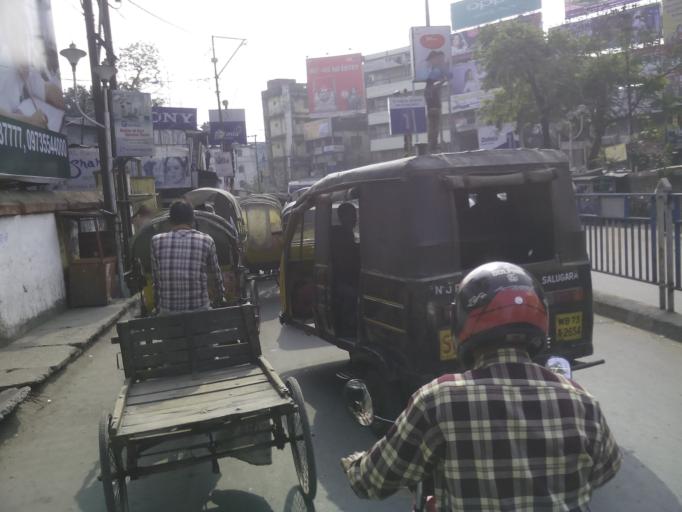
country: IN
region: West Bengal
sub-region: Darjiling
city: Shiliguri
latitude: 26.7118
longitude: 88.4262
